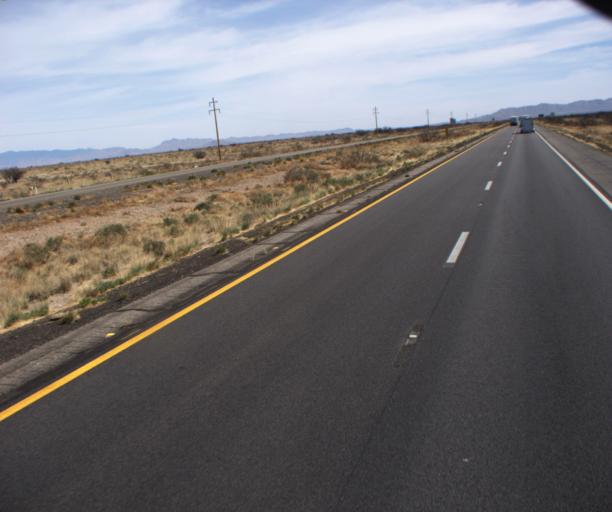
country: US
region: Arizona
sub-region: Cochise County
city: Willcox
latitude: 32.1816
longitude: -109.9406
